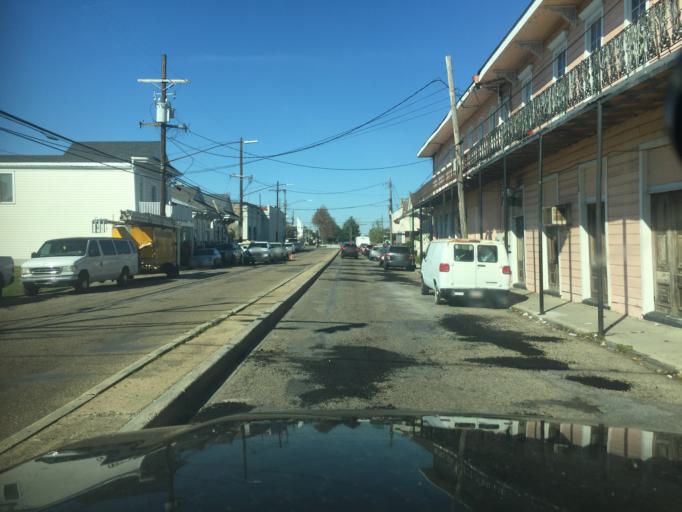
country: US
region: Louisiana
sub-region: Orleans Parish
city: New Orleans
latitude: 29.9405
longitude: -90.0780
